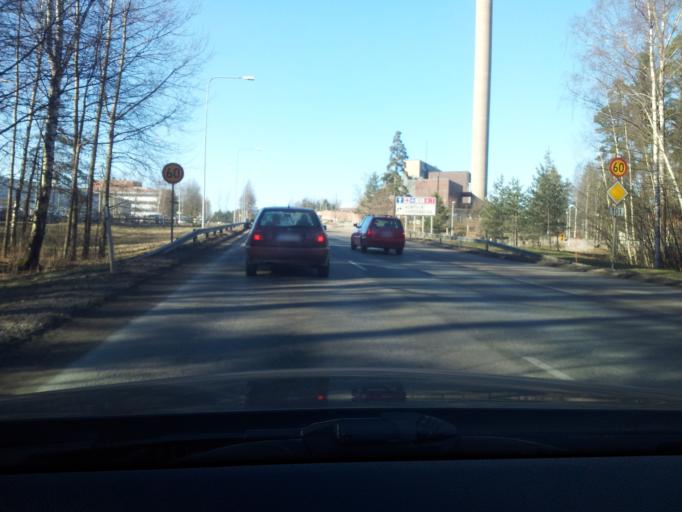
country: FI
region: Uusimaa
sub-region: Helsinki
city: Vantaa
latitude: 60.2236
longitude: 25.0806
